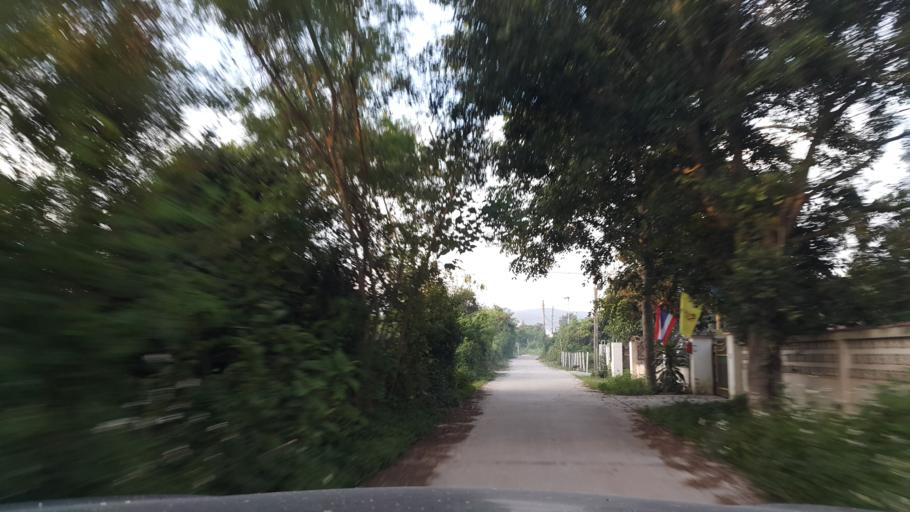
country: TH
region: Chiang Mai
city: San Sai
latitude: 18.8952
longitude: 99.0866
